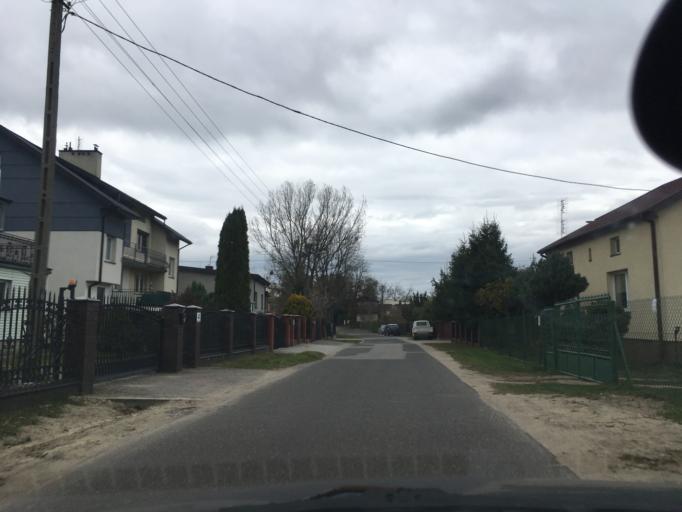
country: PL
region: Lodz Voivodeship
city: Zabia Wola
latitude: 52.0300
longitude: 20.6925
